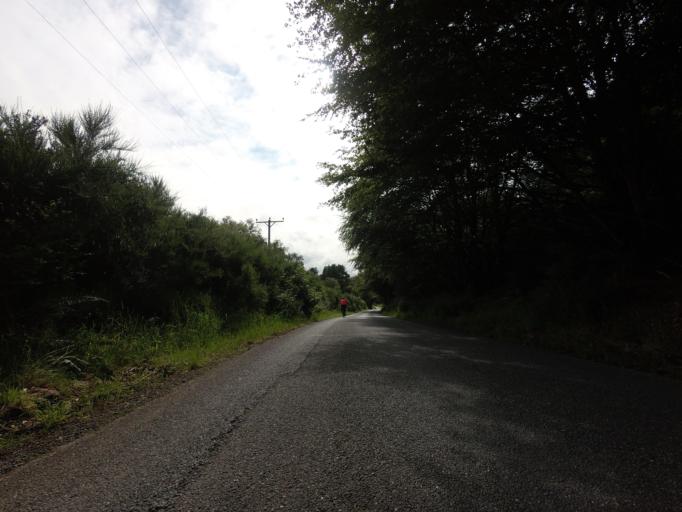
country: GB
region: Scotland
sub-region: Aberdeenshire
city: Turriff
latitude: 57.5352
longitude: -2.4082
